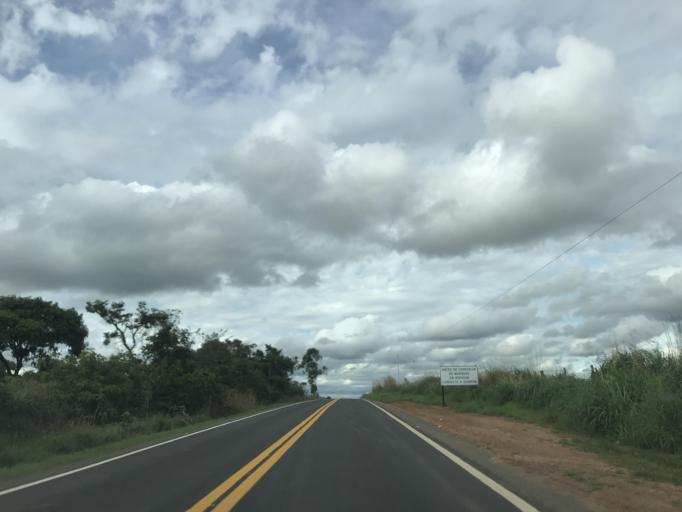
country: BR
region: Goias
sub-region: Bela Vista De Goias
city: Bela Vista de Goias
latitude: -17.1899
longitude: -48.6945
